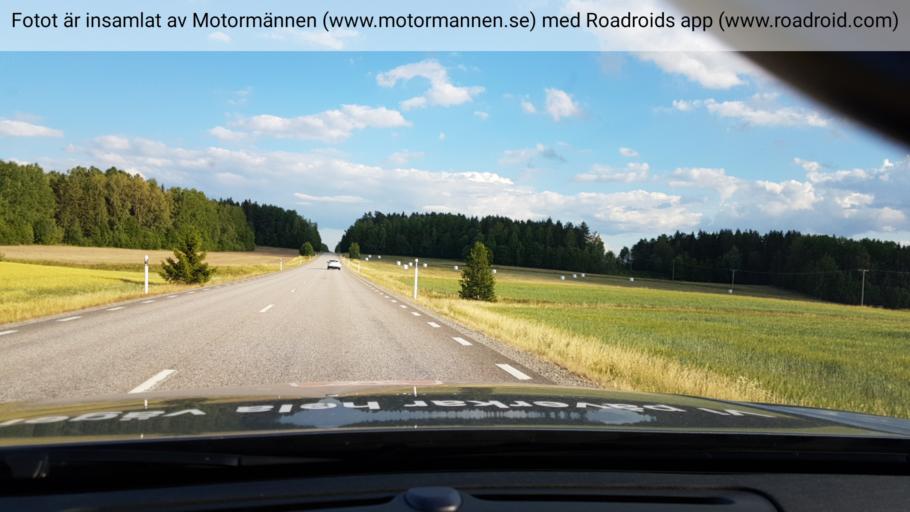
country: SE
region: Uppsala
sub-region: Heby Kommun
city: Heby
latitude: 59.9166
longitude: 16.8854
